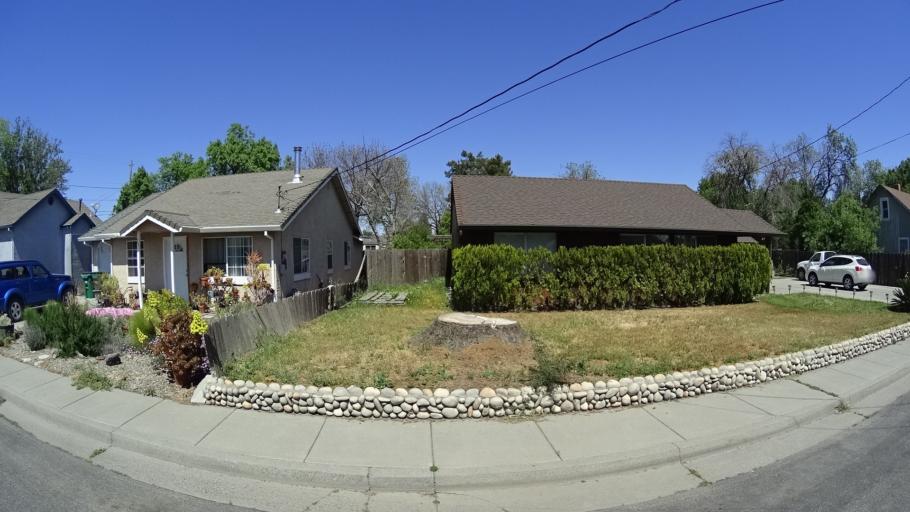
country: US
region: California
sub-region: Glenn County
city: Orland
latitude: 39.7509
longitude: -122.1845
